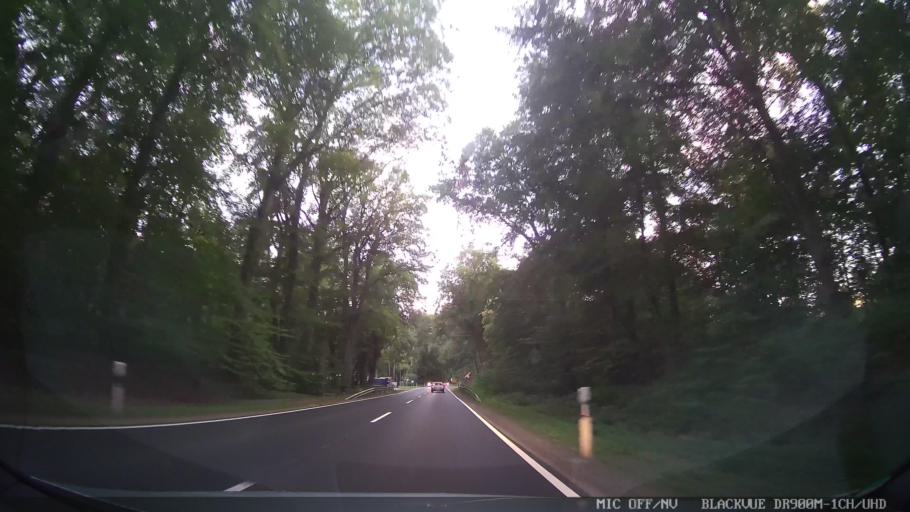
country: DE
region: Schleswig-Holstein
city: Ratekau
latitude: 53.9370
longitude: 10.7210
